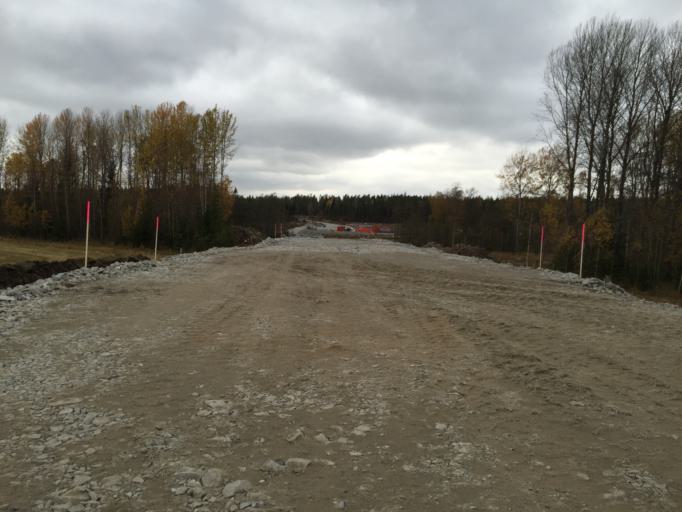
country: SE
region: Vaestmanland
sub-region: Hallstahammars Kommun
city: Hallstahammar
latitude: 59.6386
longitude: 16.2055
